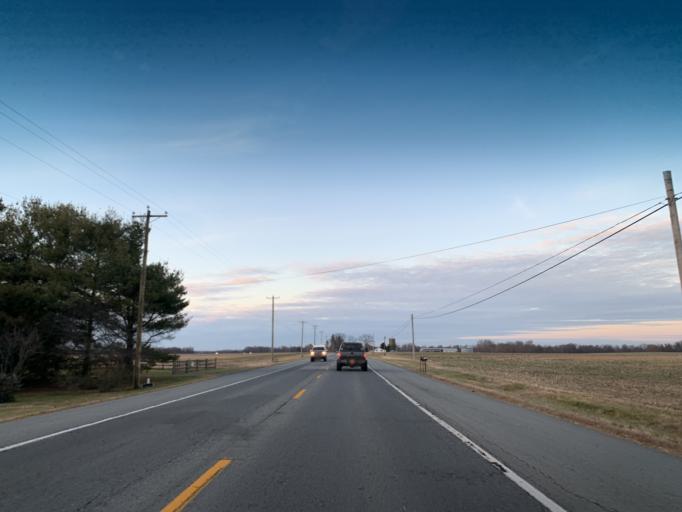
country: US
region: Delaware
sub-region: New Castle County
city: Middletown
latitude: 39.4335
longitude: -75.8612
